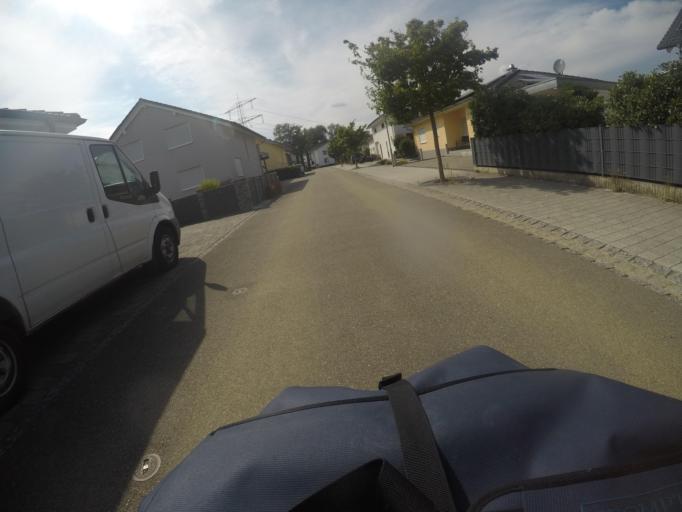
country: FR
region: Alsace
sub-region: Departement du Haut-Rhin
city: Rosenau
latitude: 47.6576
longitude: 7.5376
